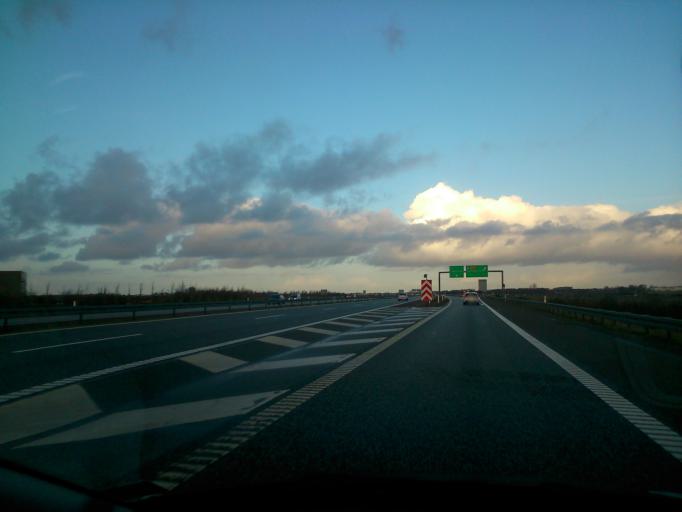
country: DK
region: Central Jutland
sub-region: Herning Kommune
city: Lind
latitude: 56.1199
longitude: 9.0119
